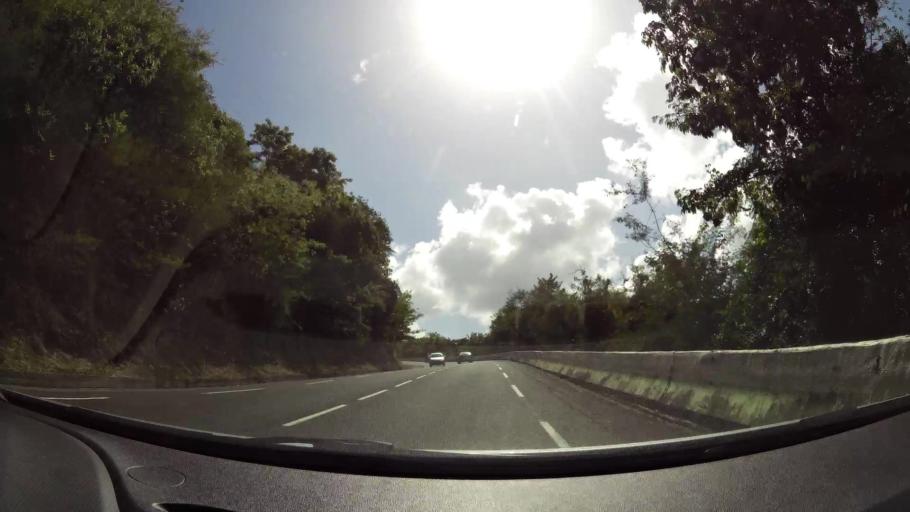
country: MQ
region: Martinique
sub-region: Martinique
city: Fort-de-France
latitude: 14.6345
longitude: -61.1294
